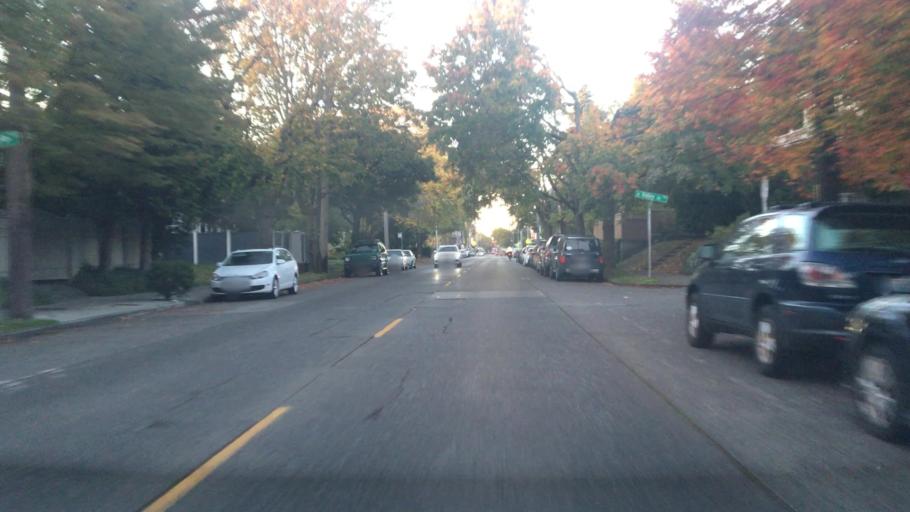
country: US
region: Washington
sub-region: King County
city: Seattle
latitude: 47.6263
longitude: -122.3126
